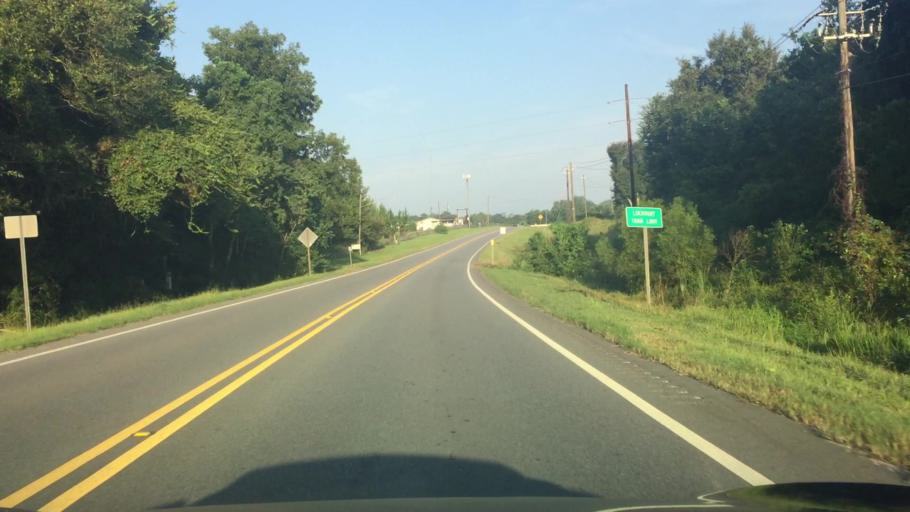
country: US
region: Alabama
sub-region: Covington County
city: Florala
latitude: 31.0087
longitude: -86.3395
